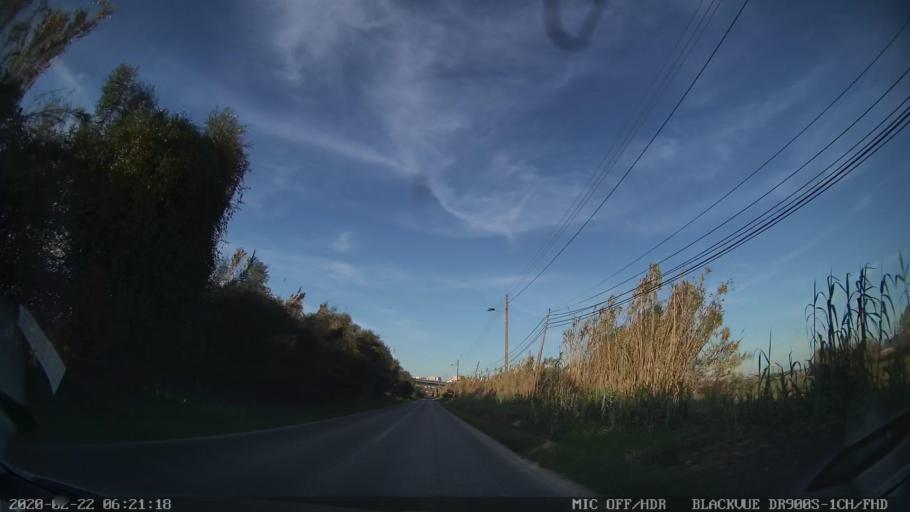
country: PT
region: Lisbon
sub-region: Alenquer
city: Carregado
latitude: 39.0162
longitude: -8.9814
